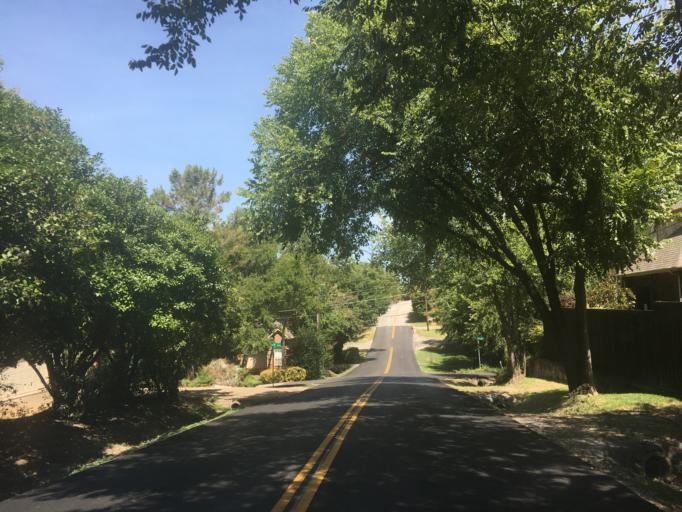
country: US
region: Texas
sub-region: Dallas County
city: Highland Park
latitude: 32.8653
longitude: -96.7246
